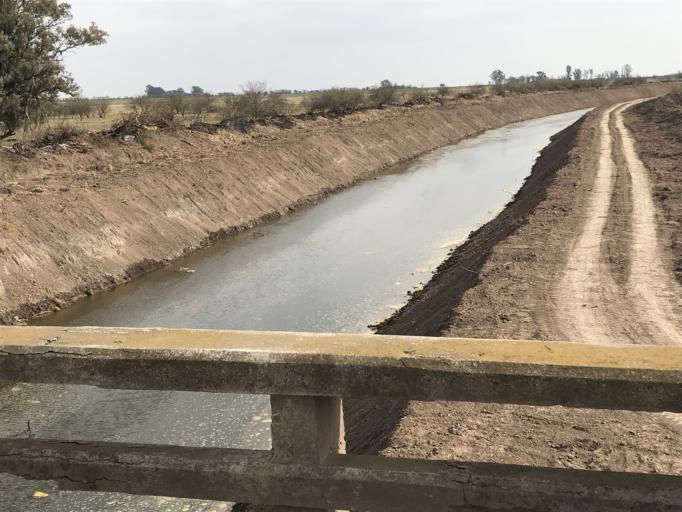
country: AR
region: Cordoba
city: General Roca
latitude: -32.7339
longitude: -61.8380
